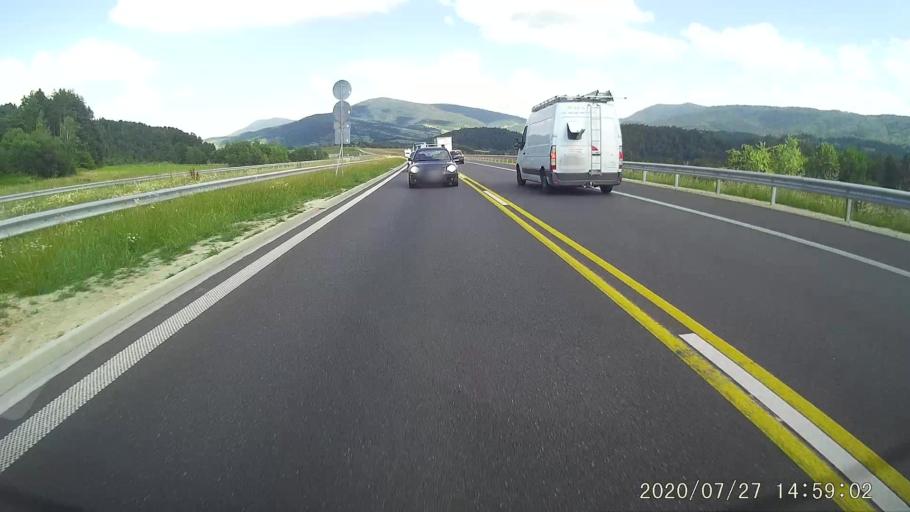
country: PL
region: Lesser Poland Voivodeship
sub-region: Powiat myslenicki
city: Krzczonow
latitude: 49.6944
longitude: 19.9201
